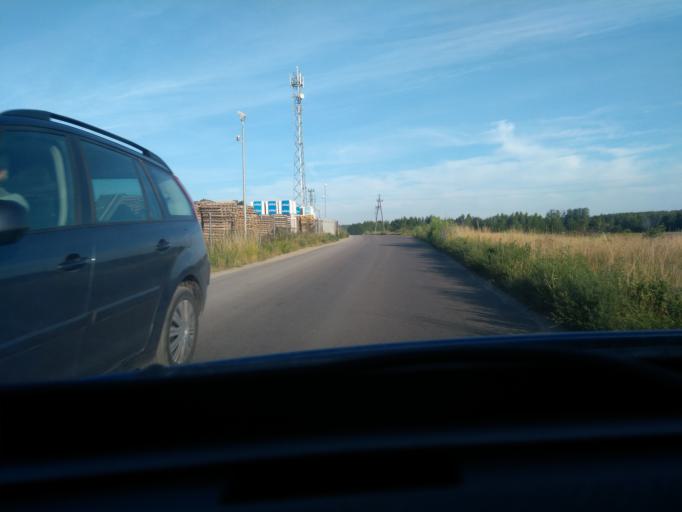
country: PL
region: Pomeranian Voivodeship
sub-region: Powiat kartuski
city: Banino
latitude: 54.3911
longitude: 18.3625
